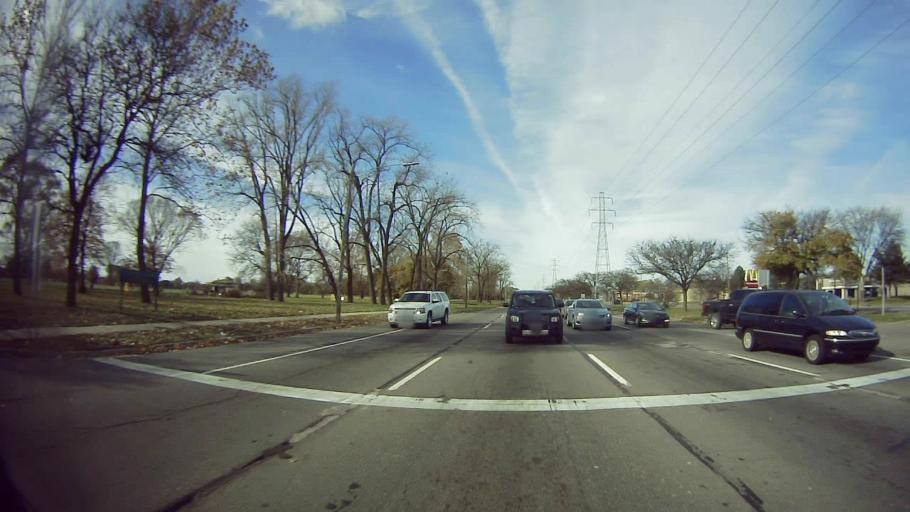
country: US
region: Michigan
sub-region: Macomb County
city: Warren
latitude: 42.4475
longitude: -83.0518
